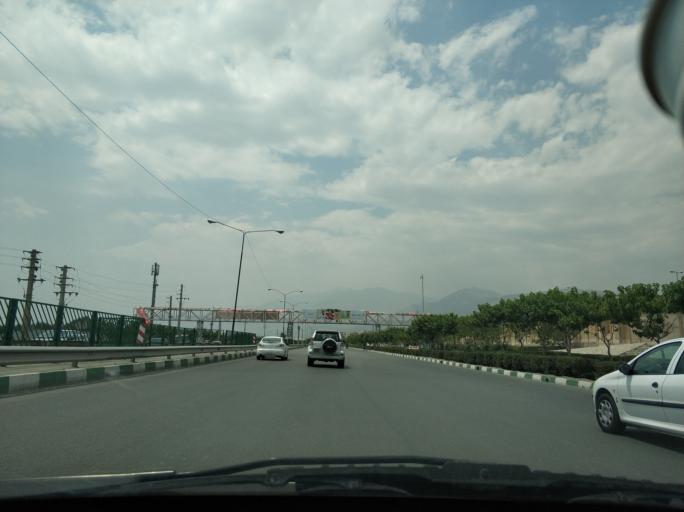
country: IR
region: Tehran
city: Tajrish
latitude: 35.7607
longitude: 51.5715
